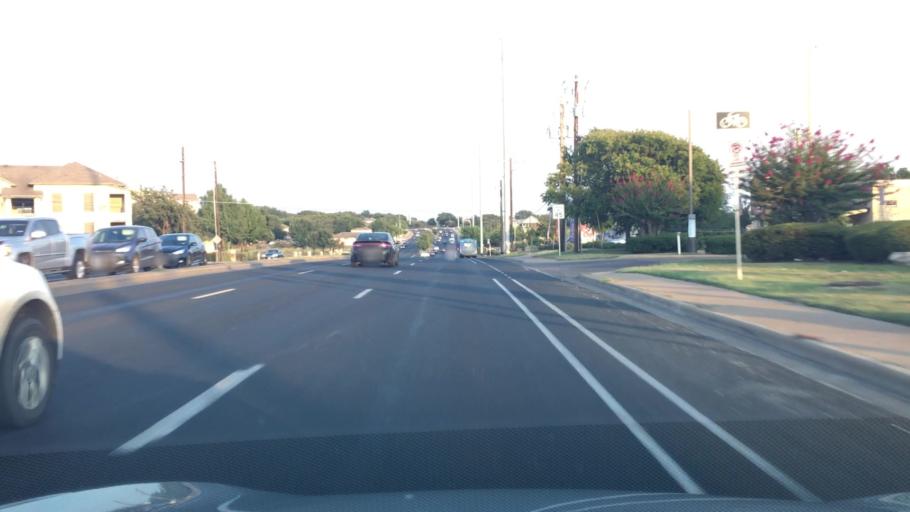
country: US
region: Texas
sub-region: Travis County
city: Onion Creek
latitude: 30.1722
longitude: -97.7994
